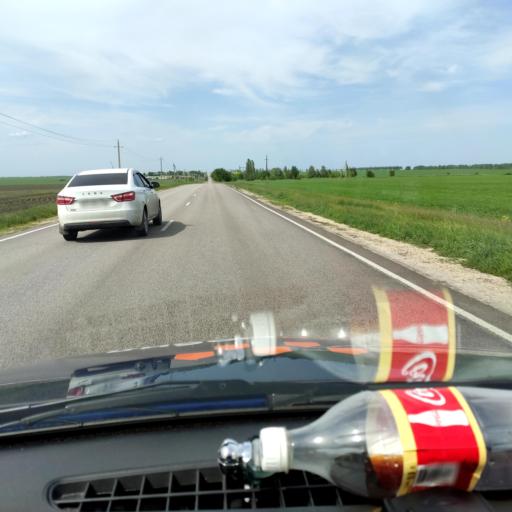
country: RU
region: Voronezj
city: Novaya Usman'
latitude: 51.5668
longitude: 39.3756
